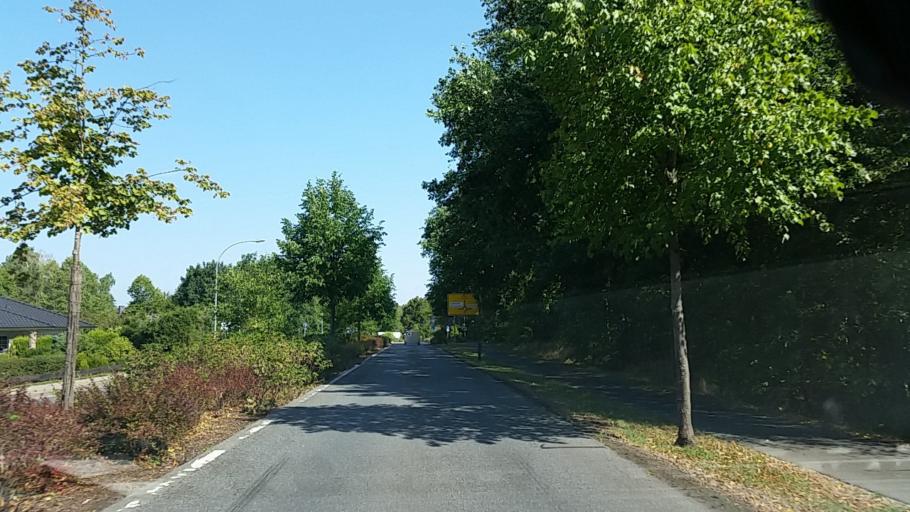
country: DE
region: Lower Saxony
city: Uelzen
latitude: 52.9317
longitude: 10.5303
